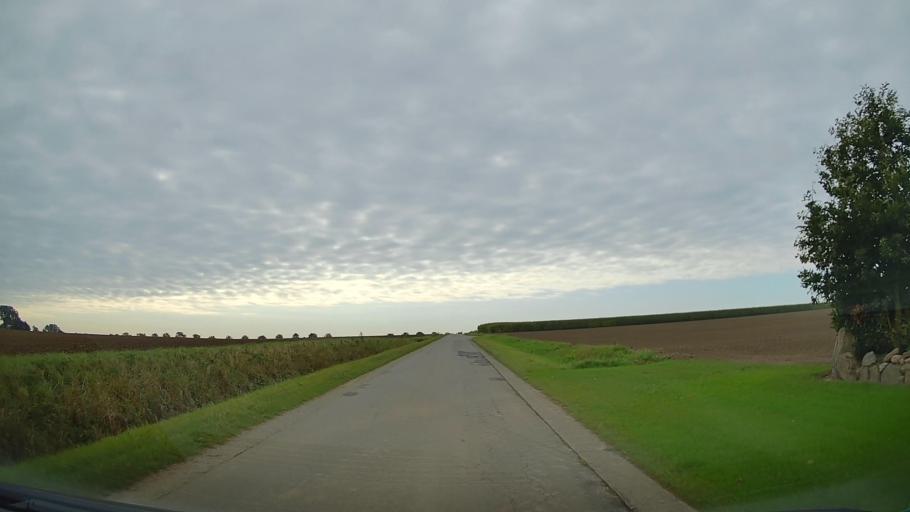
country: DE
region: Schleswig-Holstein
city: Hohenfelde
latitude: 54.3721
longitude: 10.5434
